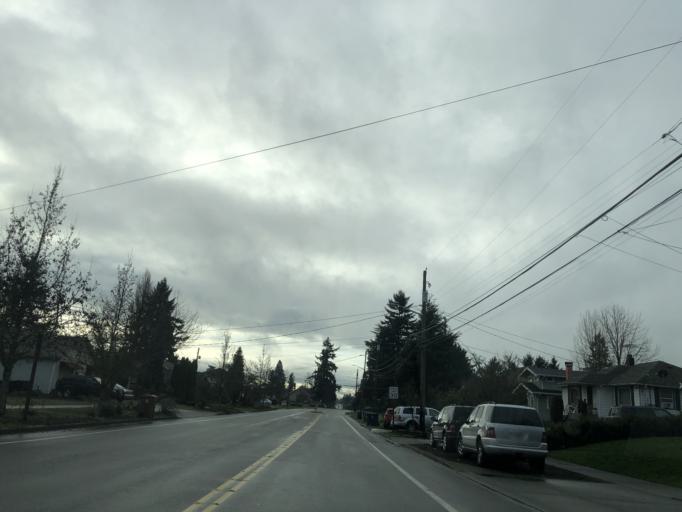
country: US
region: Washington
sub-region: Pierce County
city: Tacoma
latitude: 47.2231
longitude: -122.4579
